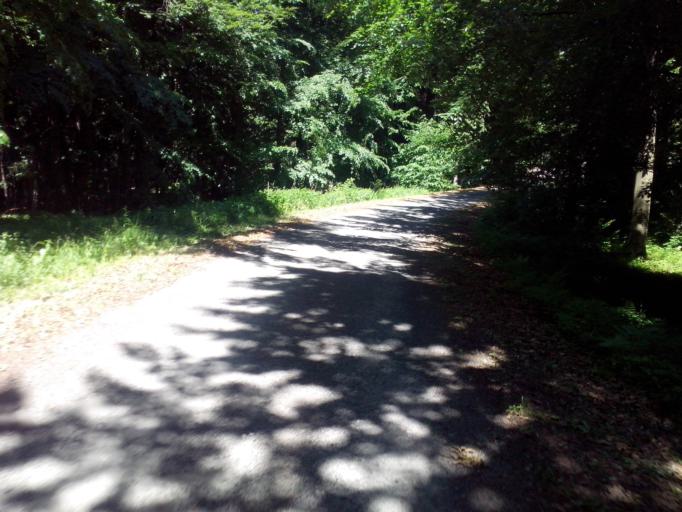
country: PL
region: Subcarpathian Voivodeship
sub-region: Powiat krosnienski
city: Leki
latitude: 49.8372
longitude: 21.6612
